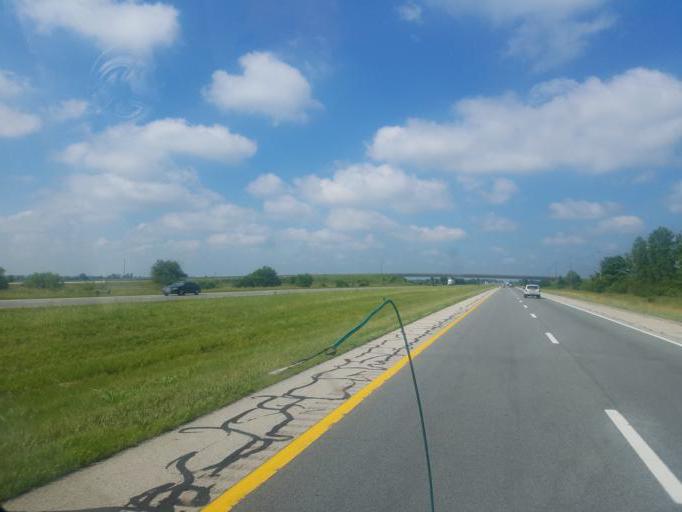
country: US
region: Ohio
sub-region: Fayette County
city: Jeffersonville
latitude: 39.6856
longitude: -83.4789
